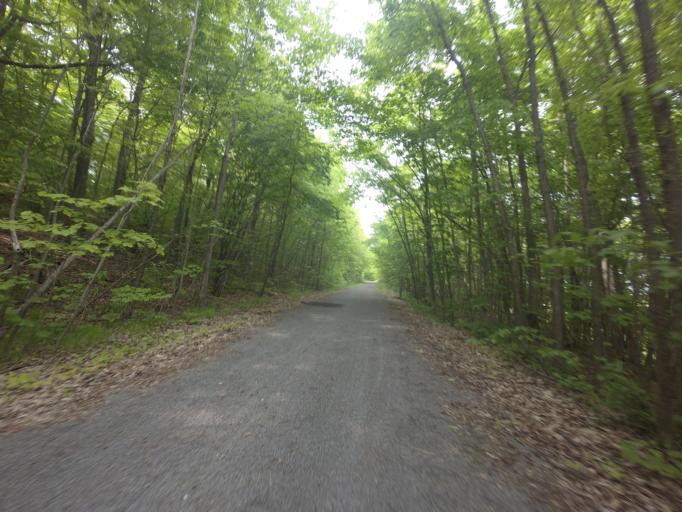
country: CA
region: Ontario
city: Kingston
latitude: 44.3935
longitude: -76.6413
